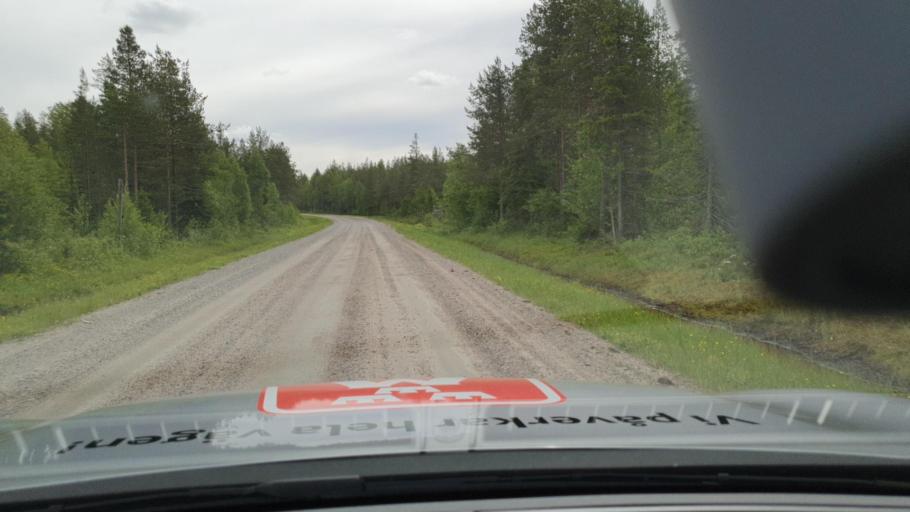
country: FI
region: Lapland
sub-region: Torniolaakso
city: Ylitornio
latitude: 65.9520
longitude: 23.7672
